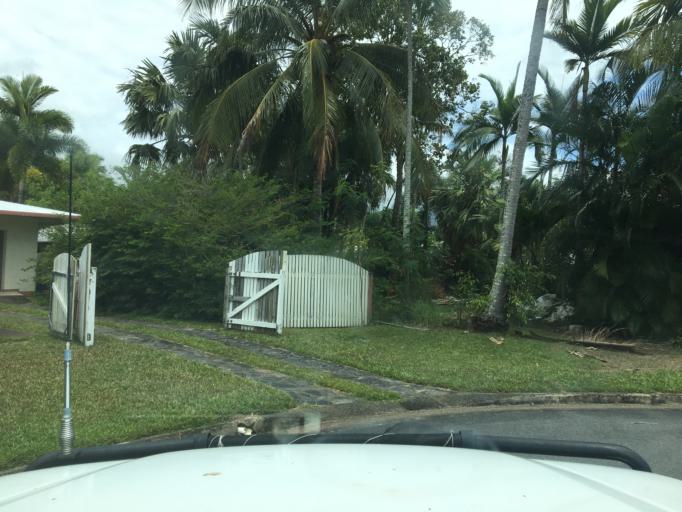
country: AU
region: Queensland
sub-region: Cairns
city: Trinity Beach
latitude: -16.7907
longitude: 145.6960
